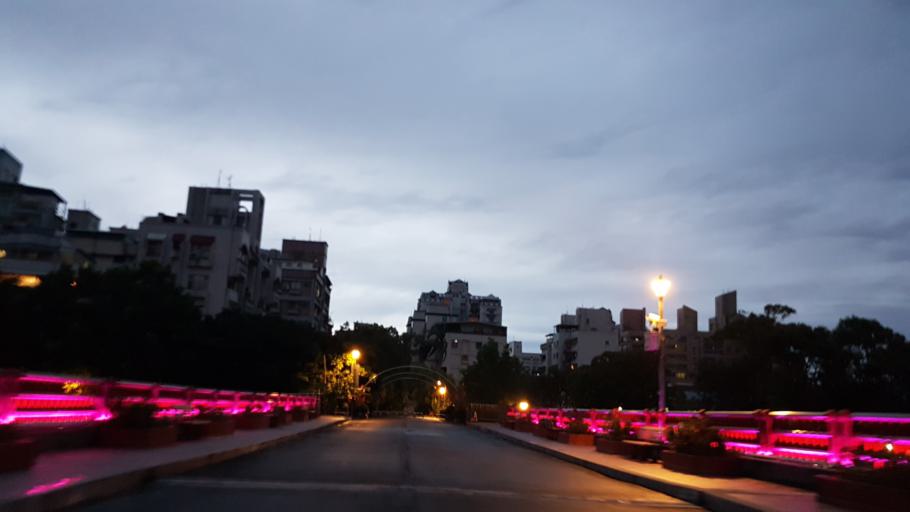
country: TW
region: Taipei
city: Taipei
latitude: 24.9764
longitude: 121.5560
